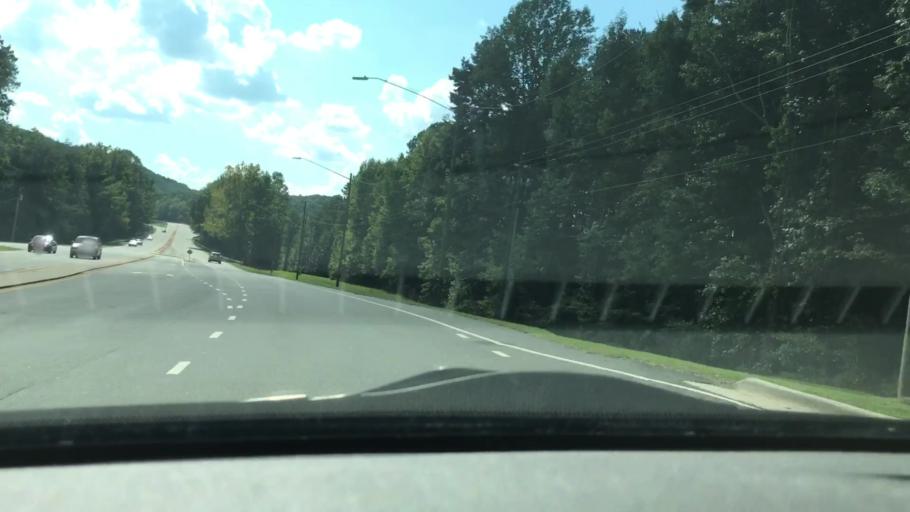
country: US
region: North Carolina
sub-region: Randolph County
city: Asheboro
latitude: 35.7355
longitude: -79.8177
